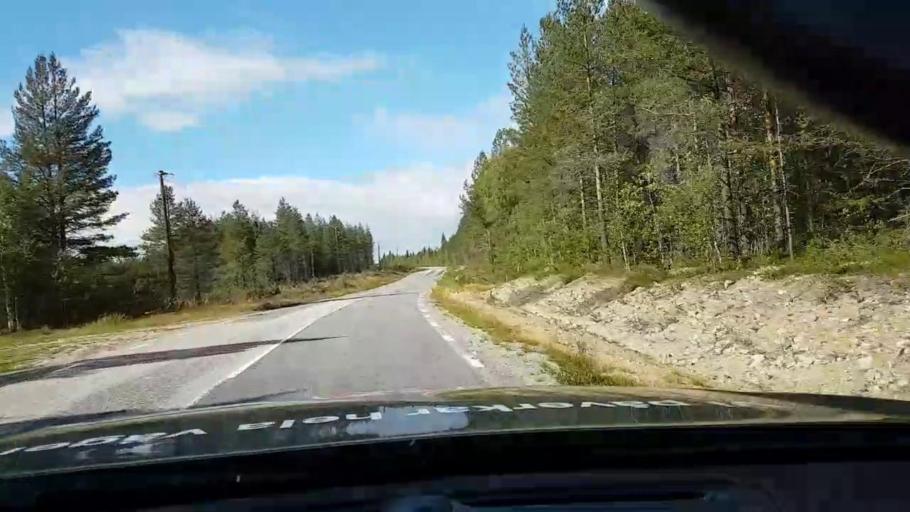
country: SE
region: Vaesterbotten
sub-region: Asele Kommun
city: Asele
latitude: 63.8177
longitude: 17.4944
